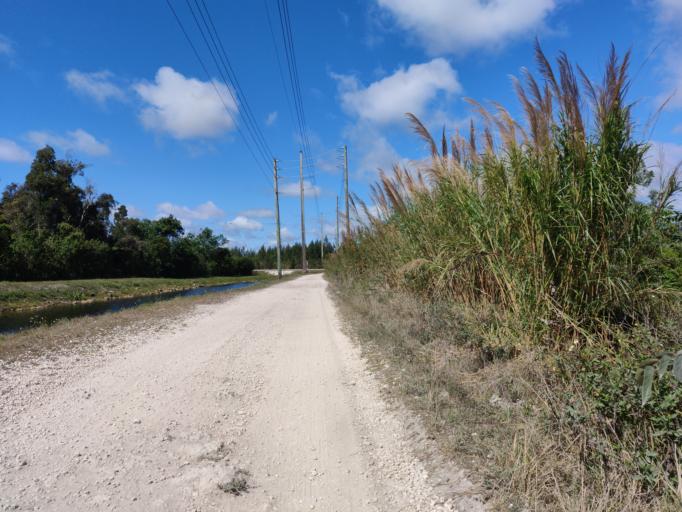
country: US
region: Florida
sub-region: Miami-Dade County
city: Kendall West
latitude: 25.7270
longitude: -80.4783
